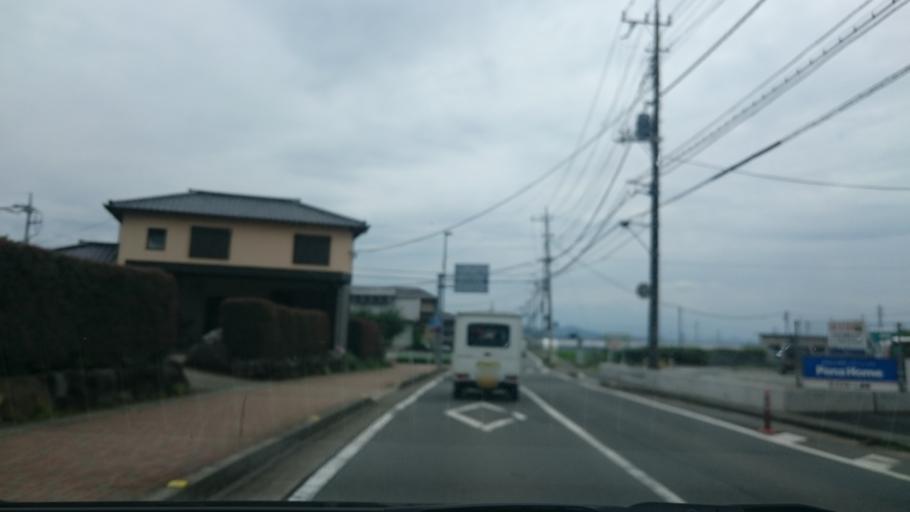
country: JP
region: Shizuoka
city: Mishima
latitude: 35.0792
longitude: 138.9468
